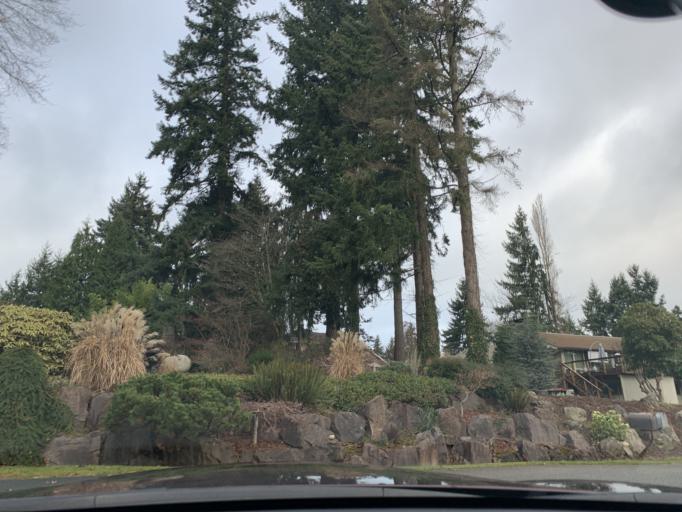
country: US
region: Washington
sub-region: King County
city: Kingsgate
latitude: 47.7358
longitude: -122.1664
